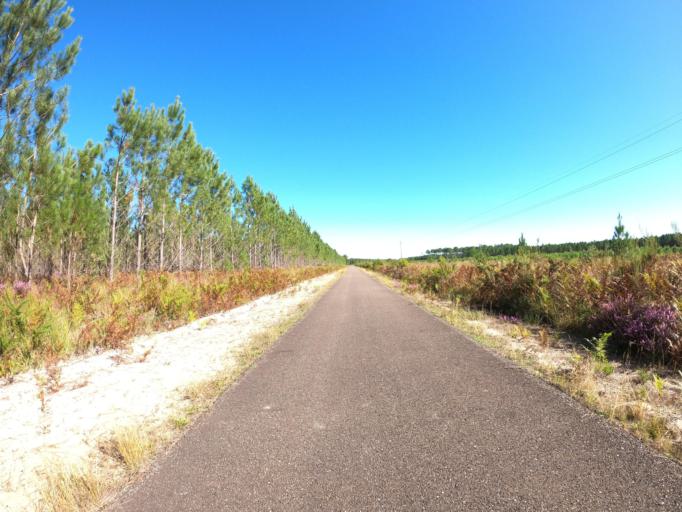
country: FR
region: Aquitaine
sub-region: Departement des Landes
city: Ychoux
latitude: 44.3403
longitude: -0.9772
